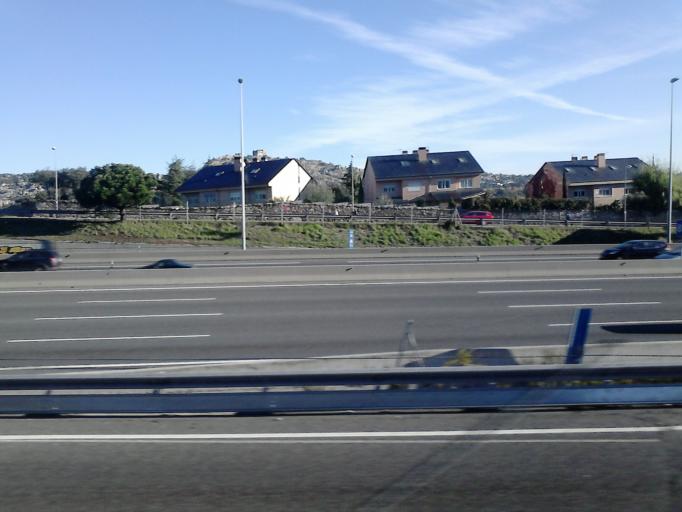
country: ES
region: Madrid
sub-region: Provincia de Madrid
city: Torrelodones
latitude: 40.5768
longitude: -3.9361
